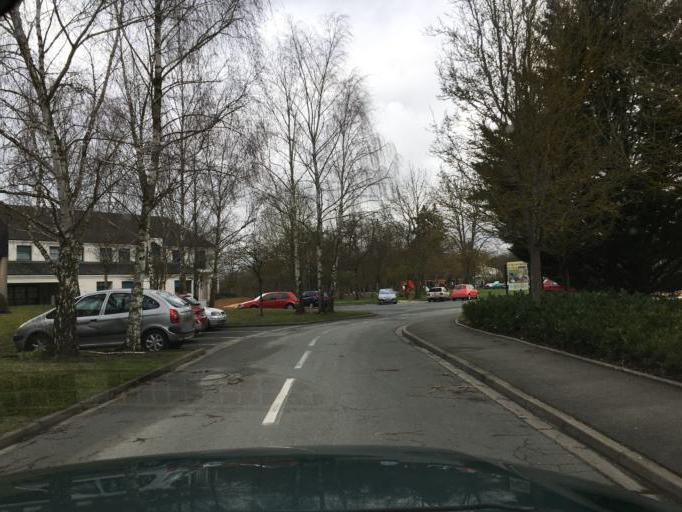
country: FR
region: Centre
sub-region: Departement du Loiret
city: Saran
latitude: 47.9519
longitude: 1.8757
